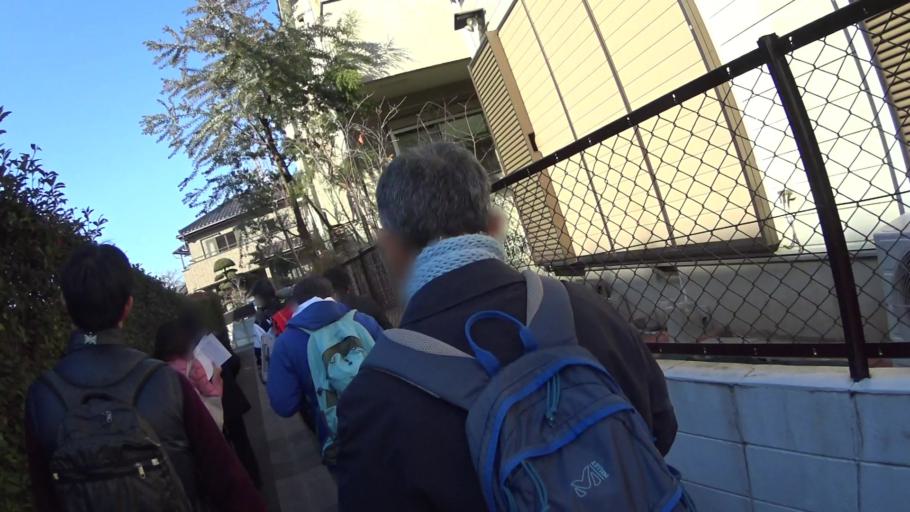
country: JP
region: Saitama
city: Saitama
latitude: 35.9062
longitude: 139.6382
